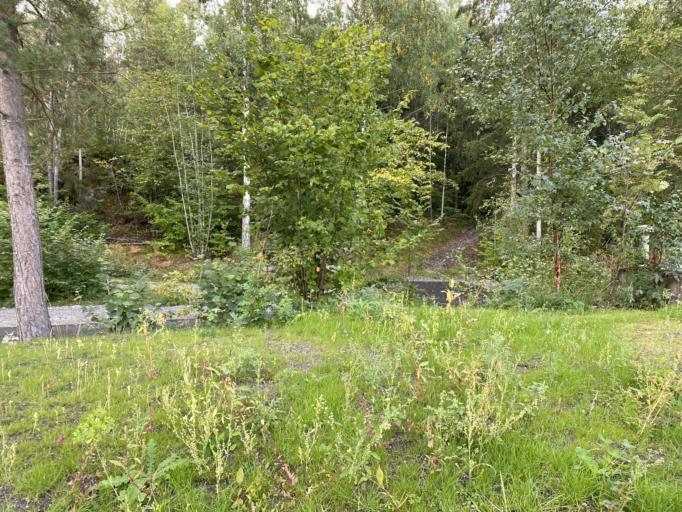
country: SE
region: Stockholm
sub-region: Salems Kommun
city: Ronninge
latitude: 59.1874
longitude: 17.7100
